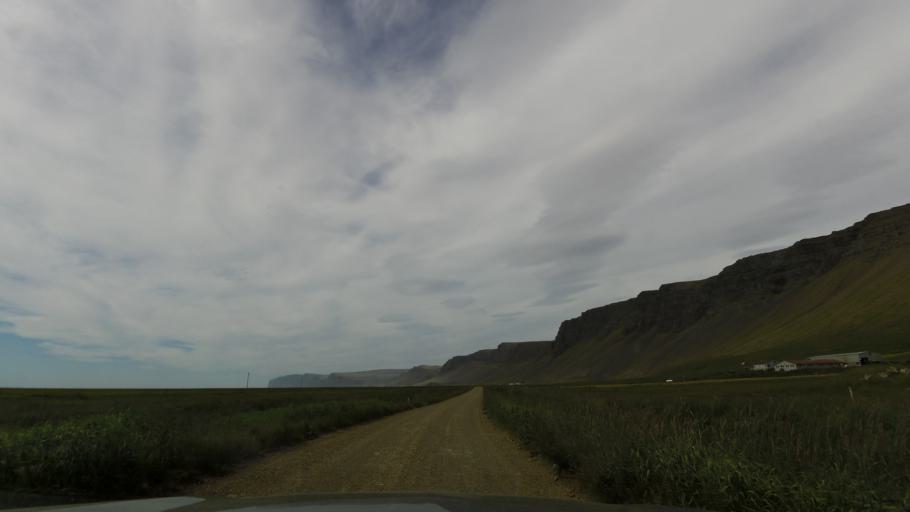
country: IS
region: West
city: Olafsvik
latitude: 65.4850
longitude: -24.0571
